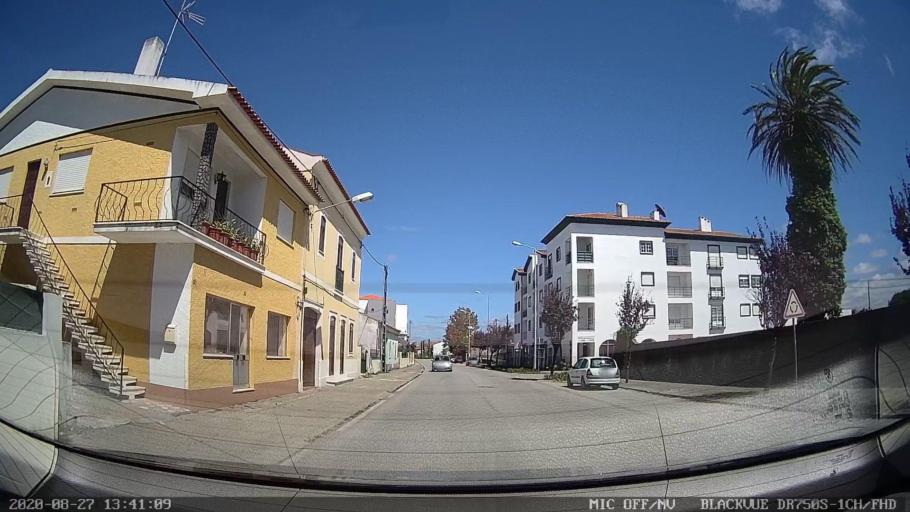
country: PT
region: Coimbra
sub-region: Mira
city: Mira
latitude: 40.4308
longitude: -8.7316
